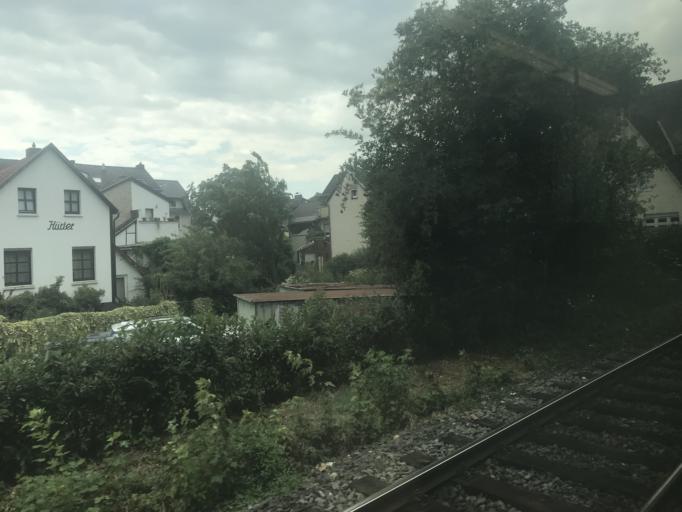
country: DE
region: North Rhine-Westphalia
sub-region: Regierungsbezirk Koln
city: Konigswinter
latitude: 50.7150
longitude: 7.1672
